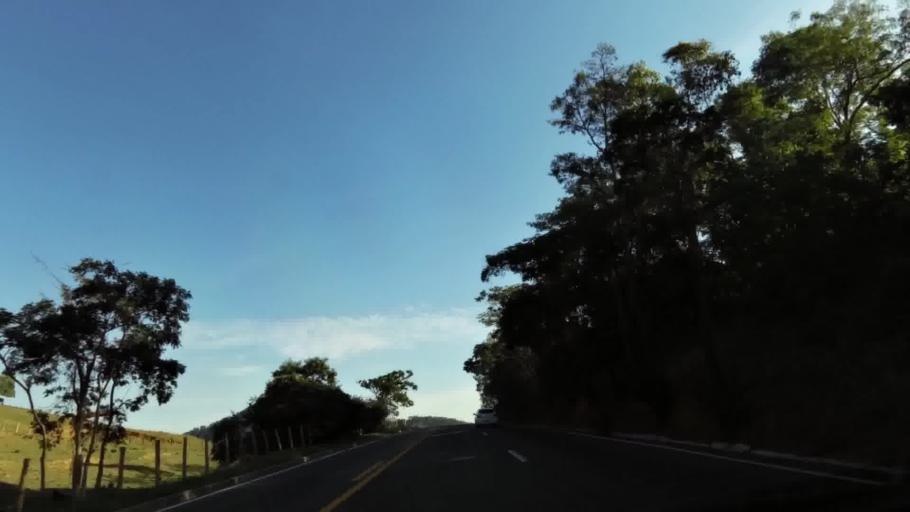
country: BR
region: Espirito Santo
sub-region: Viana
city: Viana
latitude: -20.4942
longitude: -40.4767
